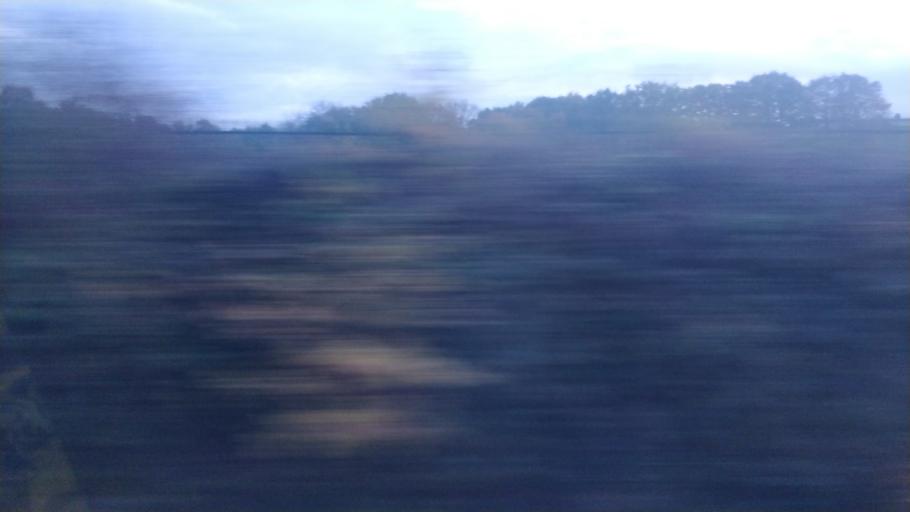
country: GB
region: England
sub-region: Borough of Wigan
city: Shevington
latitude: 53.5581
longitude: -2.6850
